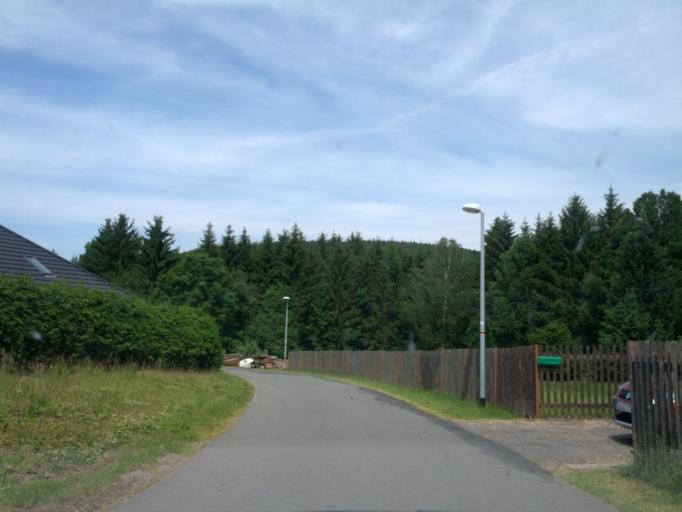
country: DE
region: Thuringia
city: Finsterbergen
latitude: 50.8378
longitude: 10.5865
